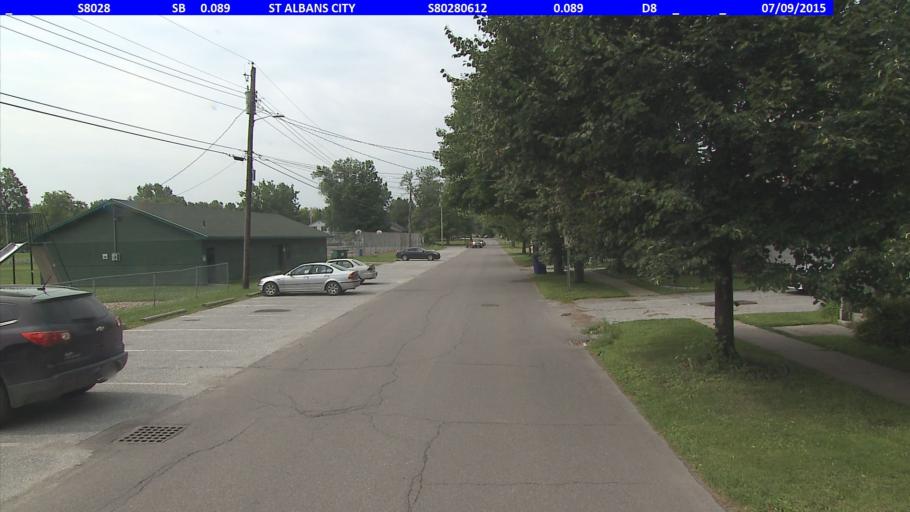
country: US
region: Vermont
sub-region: Franklin County
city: Saint Albans
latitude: 44.8101
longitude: -73.0931
